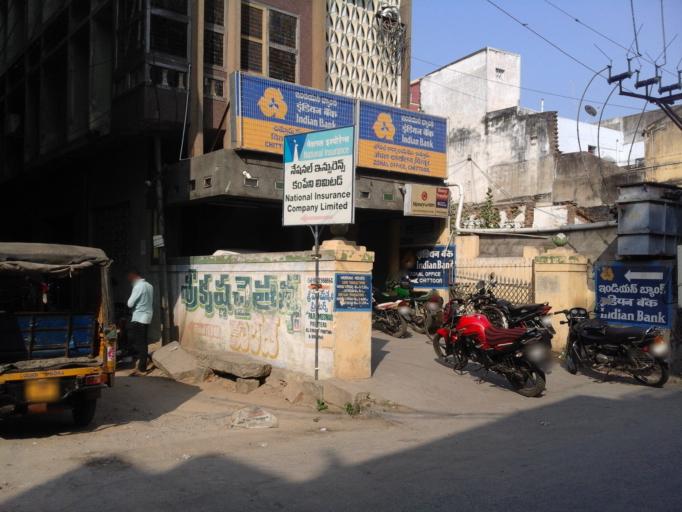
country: IN
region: Andhra Pradesh
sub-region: Chittoor
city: Chittoor
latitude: 13.2191
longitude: 79.1007
